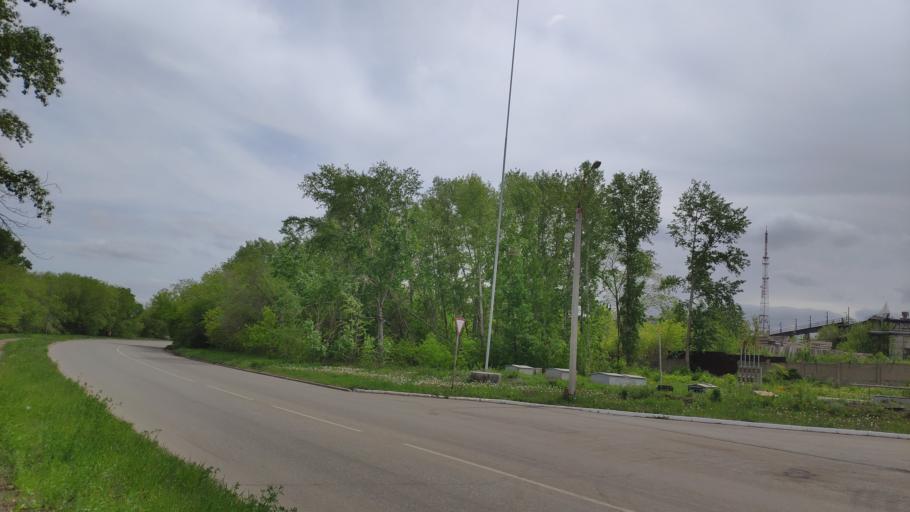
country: RU
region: Chelyabinsk
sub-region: Gorod Magnitogorsk
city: Magnitogorsk
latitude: 53.4166
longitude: 58.9548
